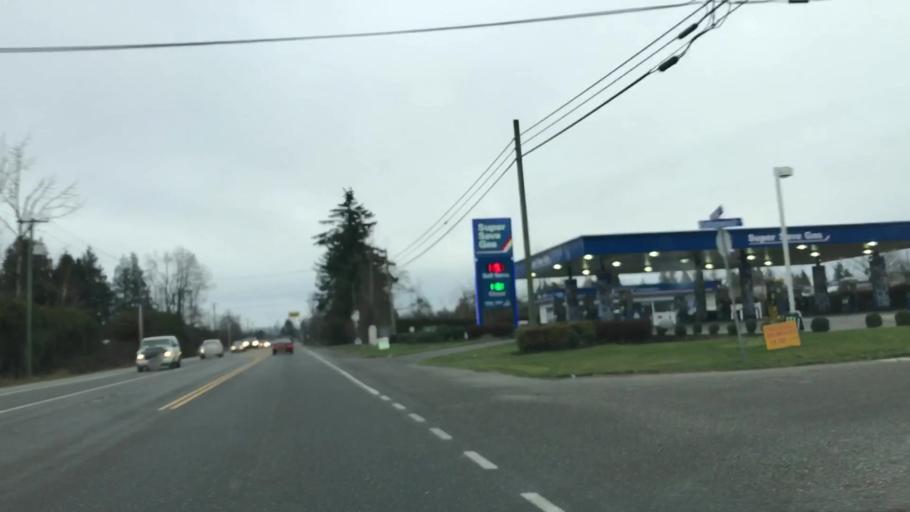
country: CA
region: British Columbia
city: Aldergrove
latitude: 49.0572
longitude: -122.4406
